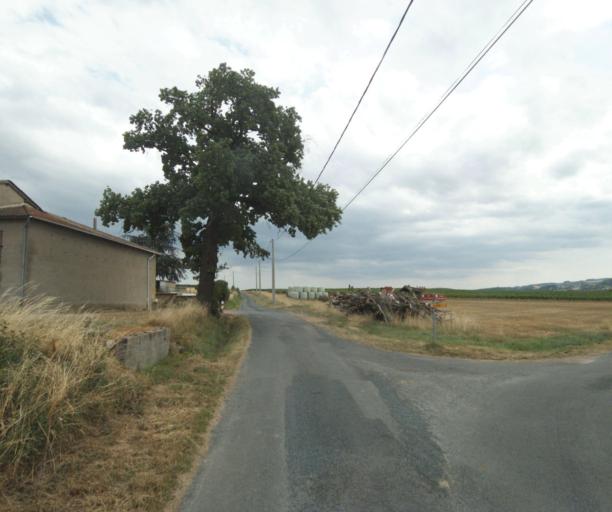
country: FR
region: Rhone-Alpes
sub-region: Departement du Rhone
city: Bully
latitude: 45.8733
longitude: 4.5576
